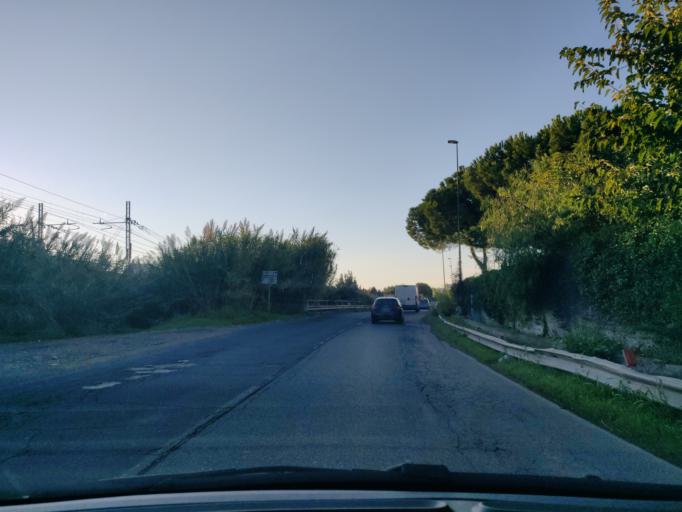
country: IT
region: Latium
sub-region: Citta metropolitana di Roma Capitale
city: Civitavecchia
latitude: 42.1118
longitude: 11.7765
